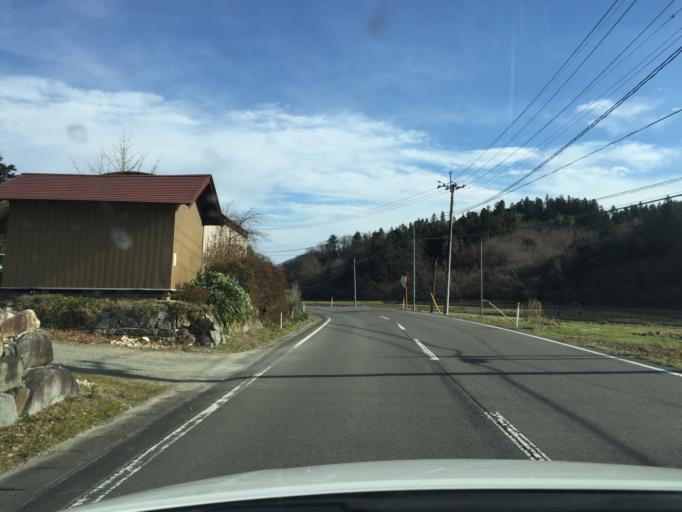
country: JP
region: Fukushima
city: Funehikimachi-funehiki
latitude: 37.2756
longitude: 140.6033
